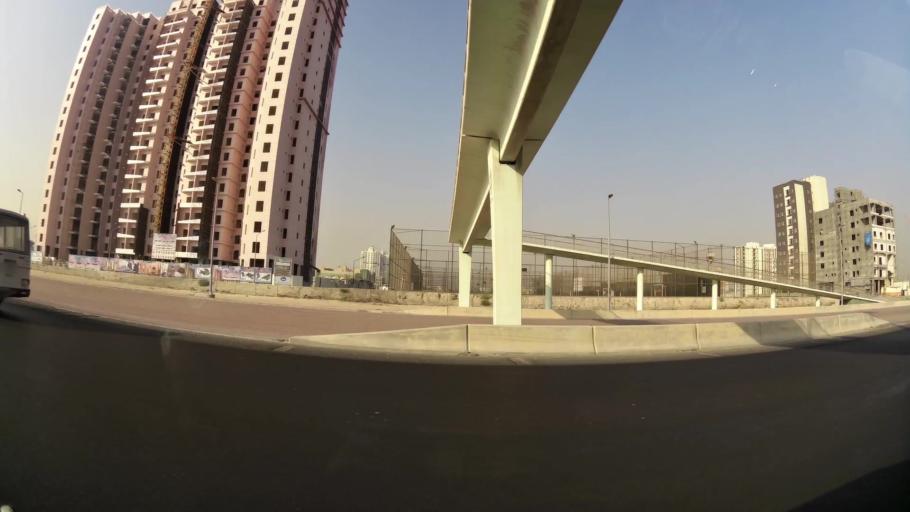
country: KW
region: Mubarak al Kabir
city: Sabah as Salim
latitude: 29.2617
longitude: 48.0871
